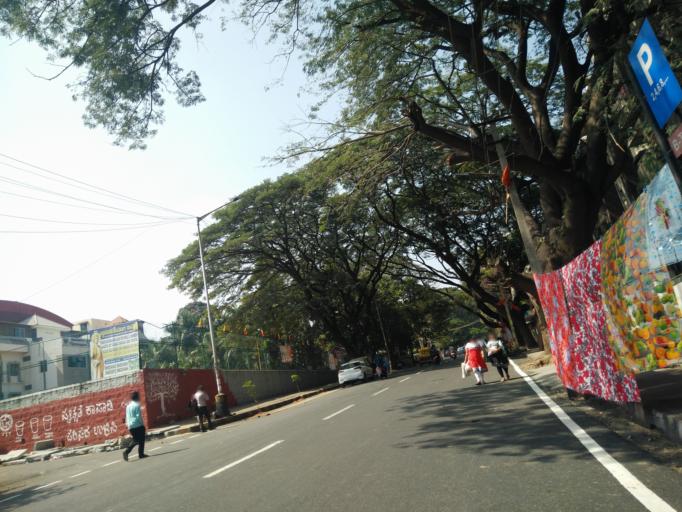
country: IN
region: Karnataka
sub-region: Bangalore Urban
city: Bangalore
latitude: 12.9678
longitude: 77.5403
